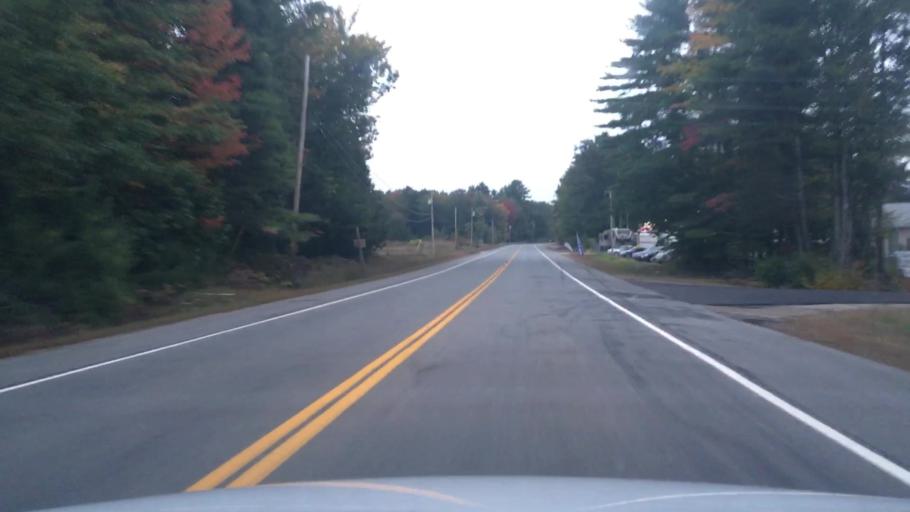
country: US
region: Maine
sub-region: York County
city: Buxton
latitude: 43.6431
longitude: -70.4920
